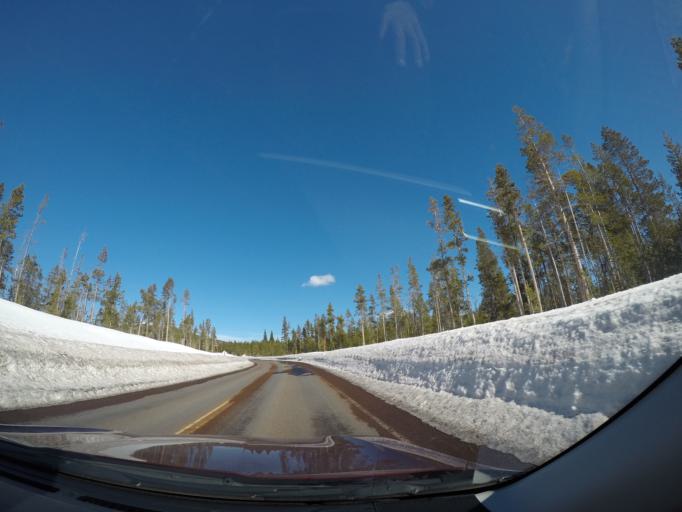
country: US
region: Oregon
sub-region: Deschutes County
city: Sunriver
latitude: 43.9616
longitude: -121.6155
